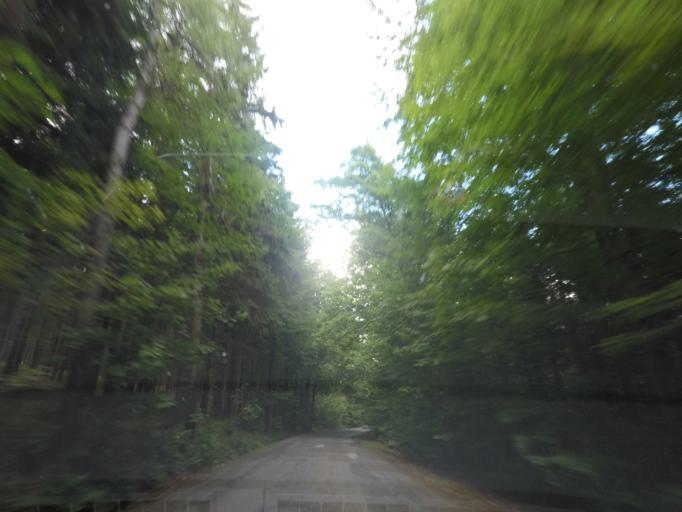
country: CZ
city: Radvanice
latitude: 50.6069
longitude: 16.0585
